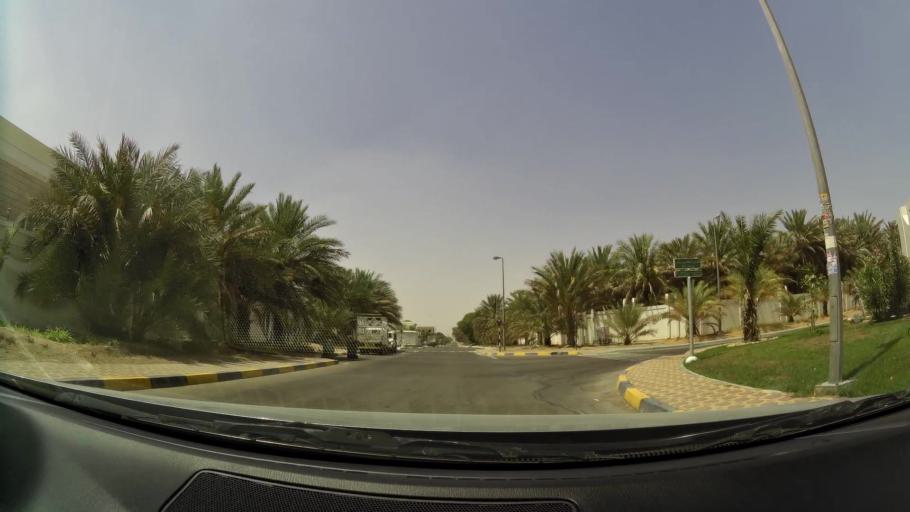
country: AE
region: Abu Dhabi
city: Al Ain
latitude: 24.2541
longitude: 55.6989
